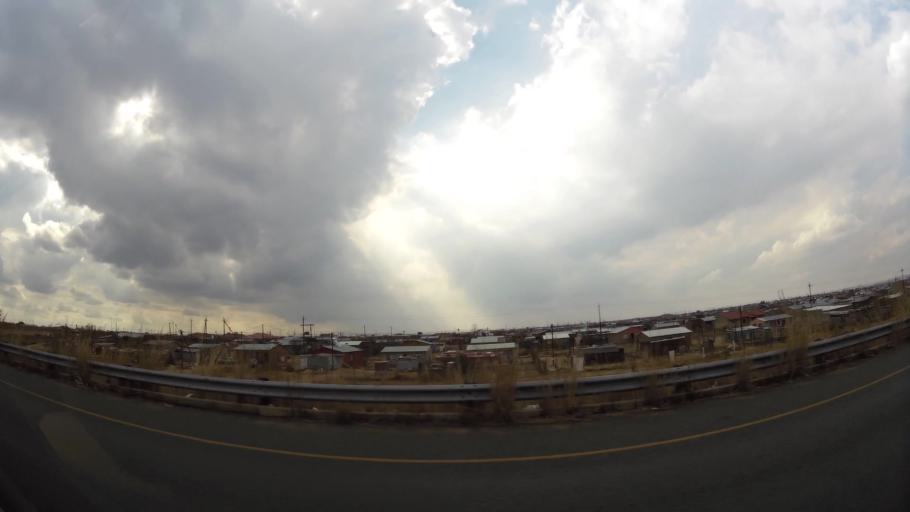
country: ZA
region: Orange Free State
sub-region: Fezile Dabi District Municipality
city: Sasolburg
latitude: -26.8660
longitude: 27.8908
